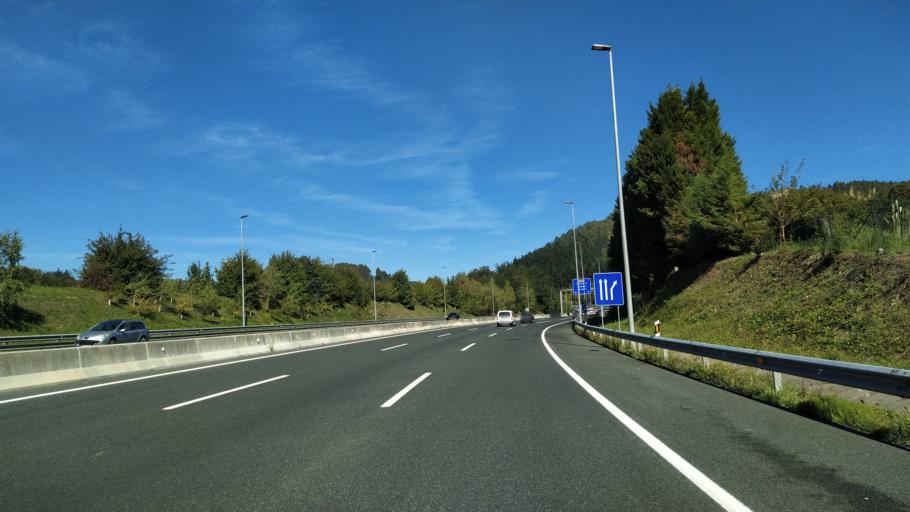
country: ES
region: Basque Country
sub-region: Bizkaia
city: Derio
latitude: 43.3020
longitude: -2.8825
